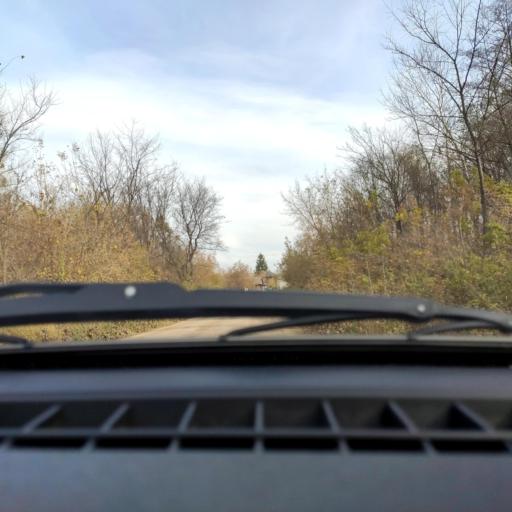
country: RU
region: Bashkortostan
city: Ufa
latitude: 54.7839
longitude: 56.1832
